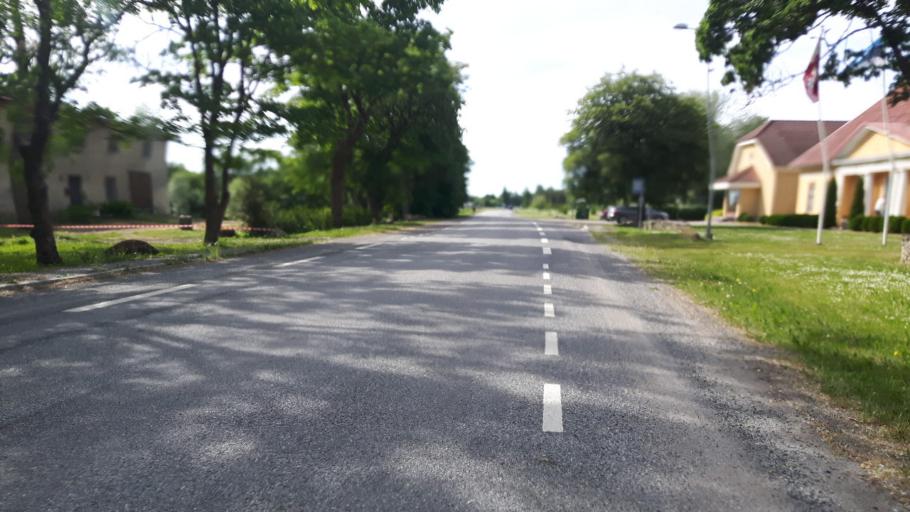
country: EE
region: Harju
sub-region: Raasiku vald
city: Raasiku
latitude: 59.4399
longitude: 25.1457
